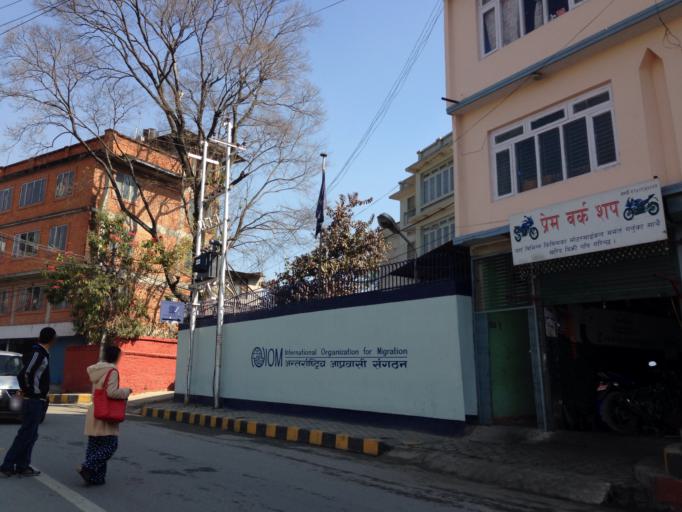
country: NP
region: Central Region
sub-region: Bagmati Zone
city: Kathmandu
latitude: 27.7284
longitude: 85.3309
